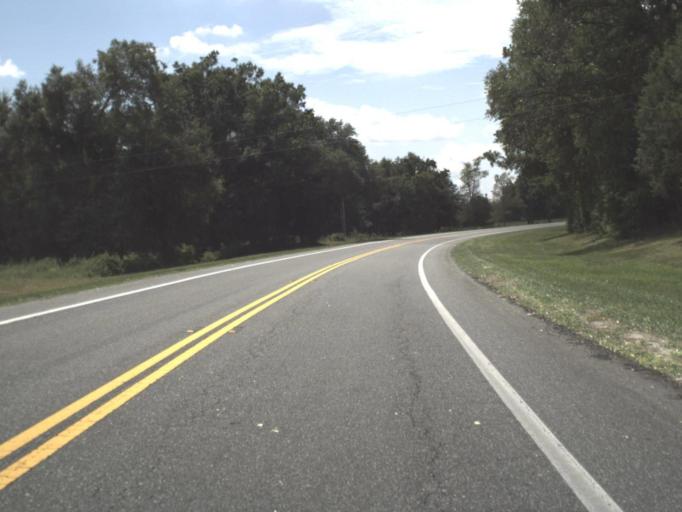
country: US
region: Florida
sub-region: Suwannee County
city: Live Oak
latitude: 30.1527
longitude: -82.9500
